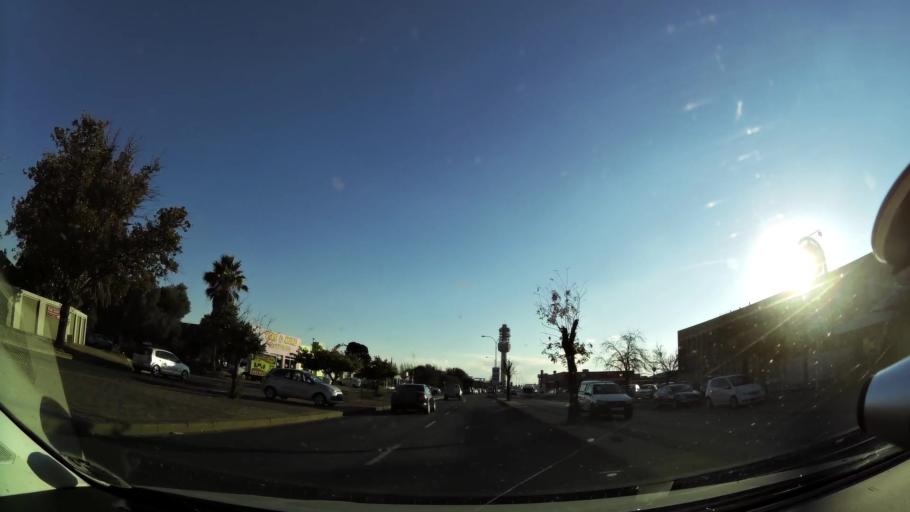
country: ZA
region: Northern Cape
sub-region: Frances Baard District Municipality
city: Kimberley
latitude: -28.7440
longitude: 24.7576
